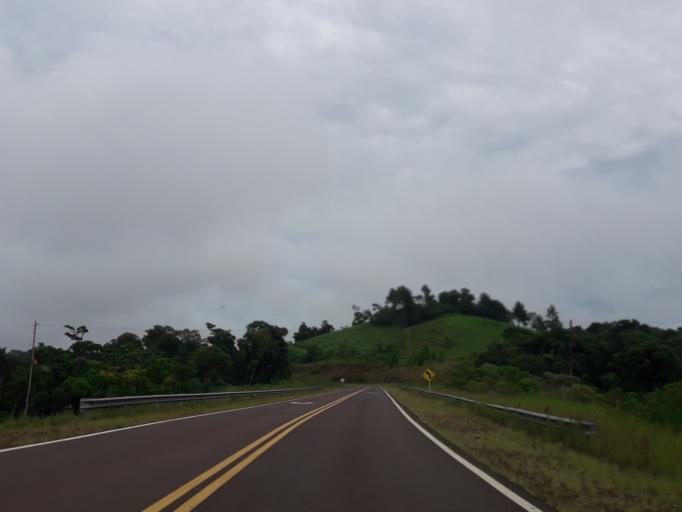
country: AR
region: Misiones
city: Bernardo de Irigoyen
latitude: -26.3964
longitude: -53.8106
